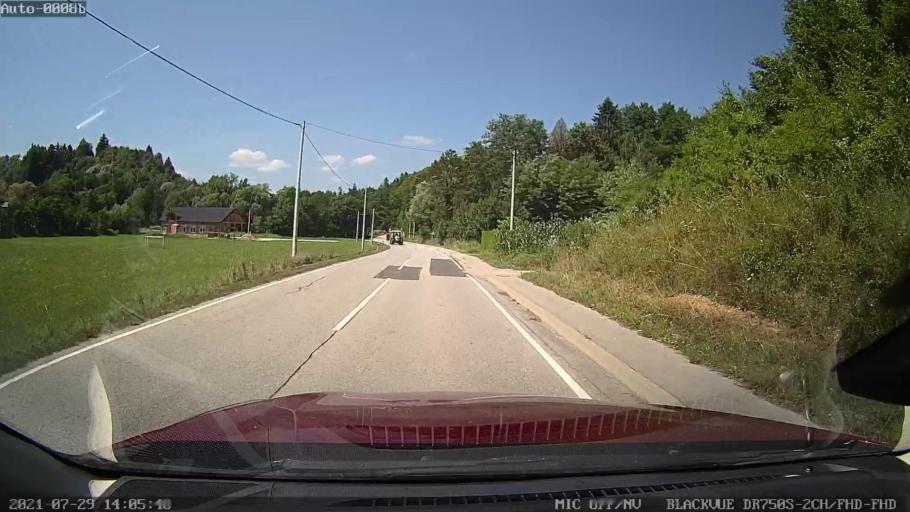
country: HR
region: Varazdinska
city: Lepoglava
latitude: 46.2527
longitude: 15.9565
